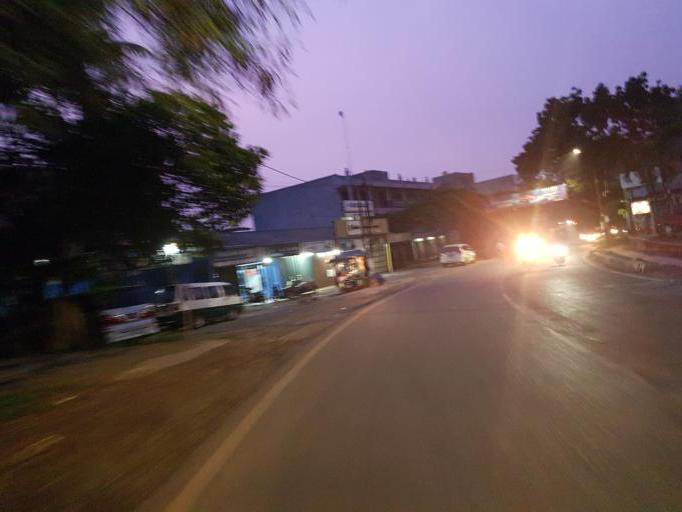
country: ID
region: West Java
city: Serpong
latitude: -6.3144
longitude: 106.6609
